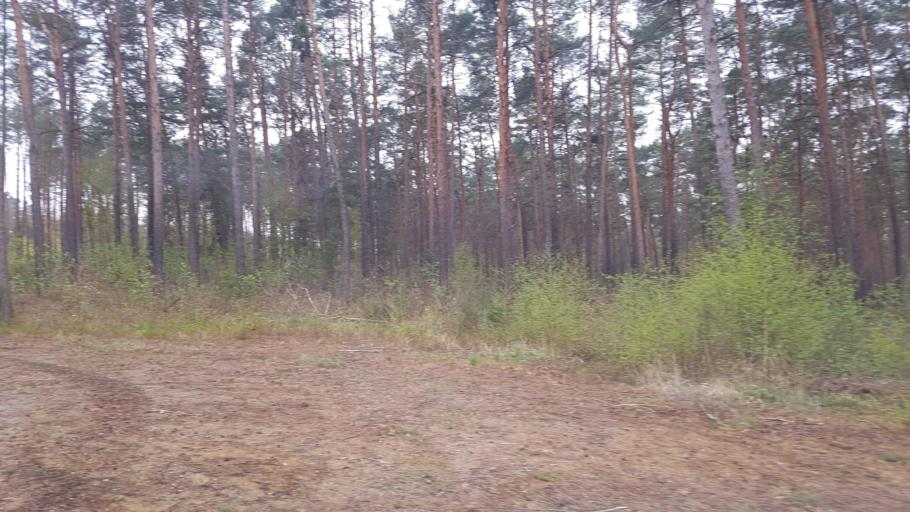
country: DE
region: Brandenburg
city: Ihlow
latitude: 51.9709
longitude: 13.3416
